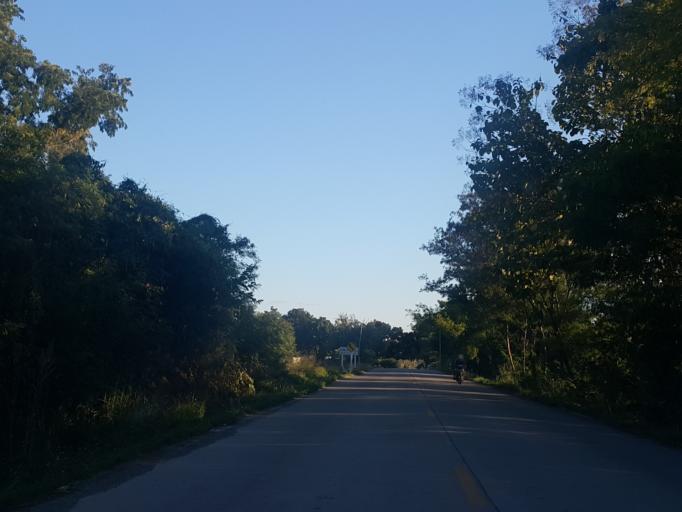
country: TH
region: Chiang Mai
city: San Sai
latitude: 18.8830
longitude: 99.1563
